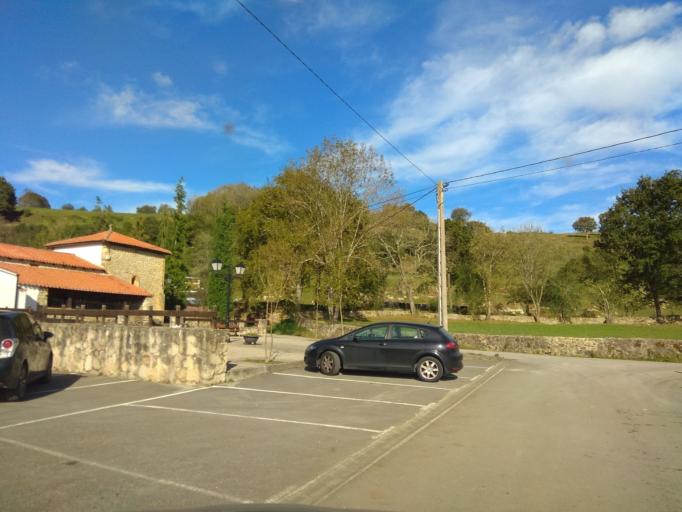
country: ES
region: Cantabria
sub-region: Provincia de Cantabria
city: San Vicente de la Barquera
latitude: 43.3294
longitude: -4.4830
